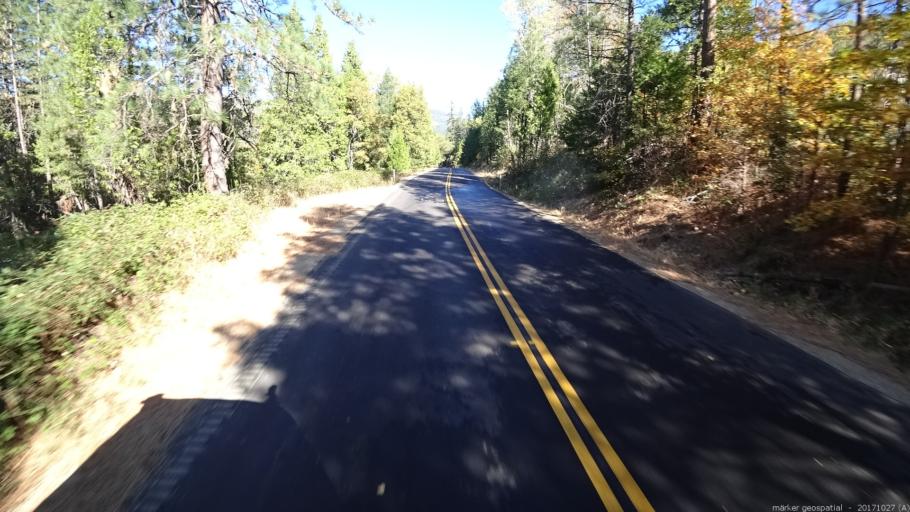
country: US
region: California
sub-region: Shasta County
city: Shingletown
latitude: 40.6753
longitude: -121.8771
